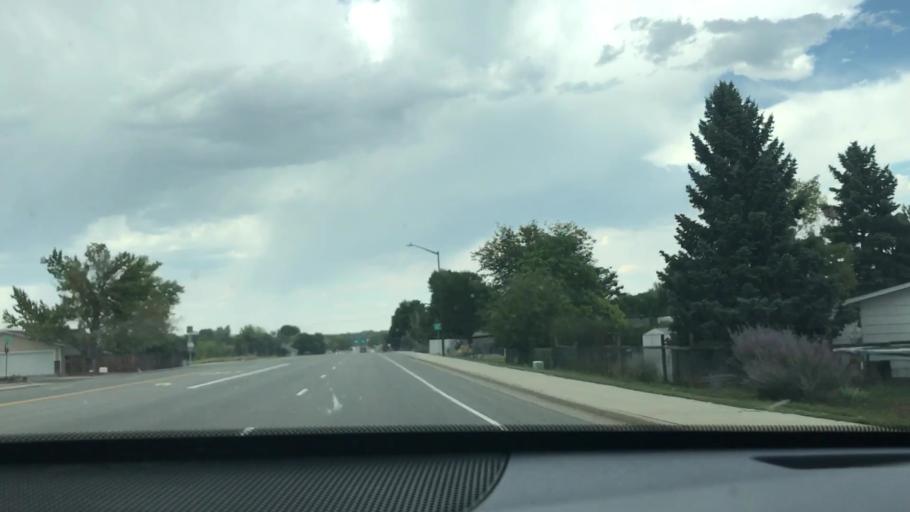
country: US
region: Colorado
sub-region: Larimer County
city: Loveland
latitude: 40.3793
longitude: -105.1159
